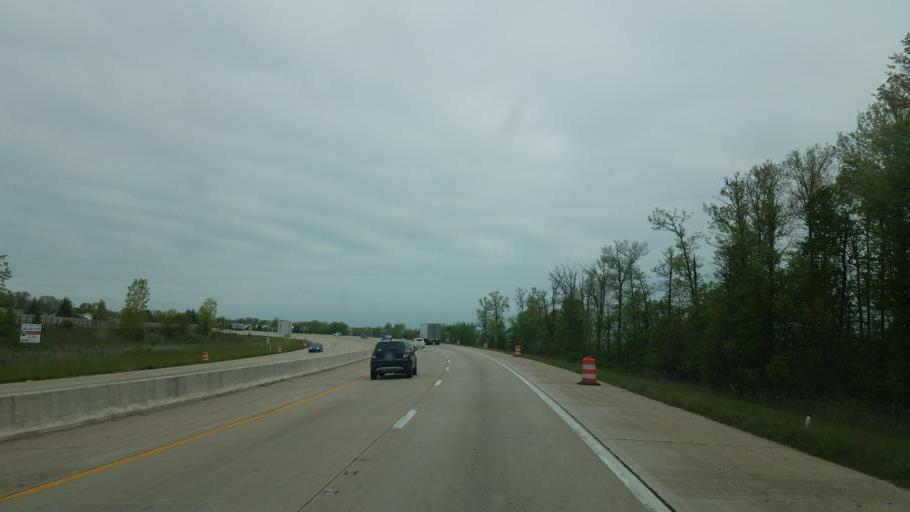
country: US
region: Indiana
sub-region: Allen County
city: Leo-Cedarville
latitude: 41.1505
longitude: -85.0157
